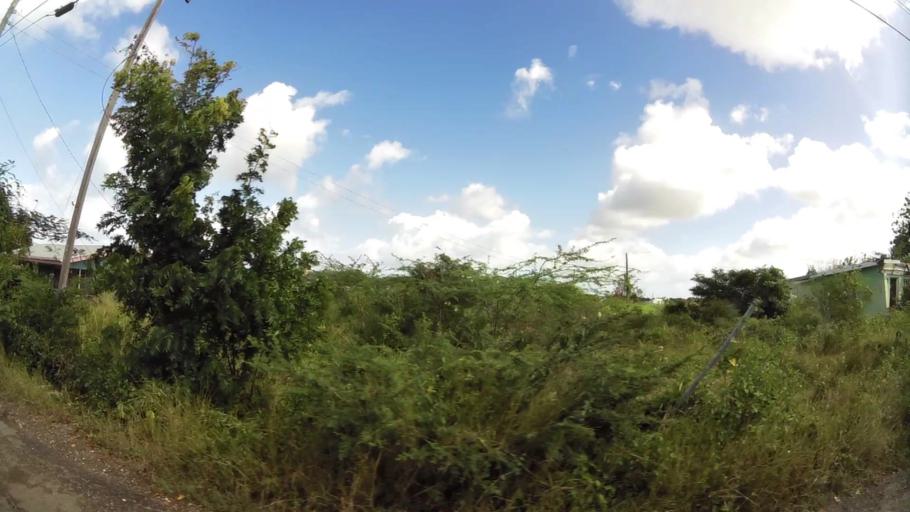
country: AG
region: Saint John
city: Saint John's
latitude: 17.1400
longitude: -61.8568
